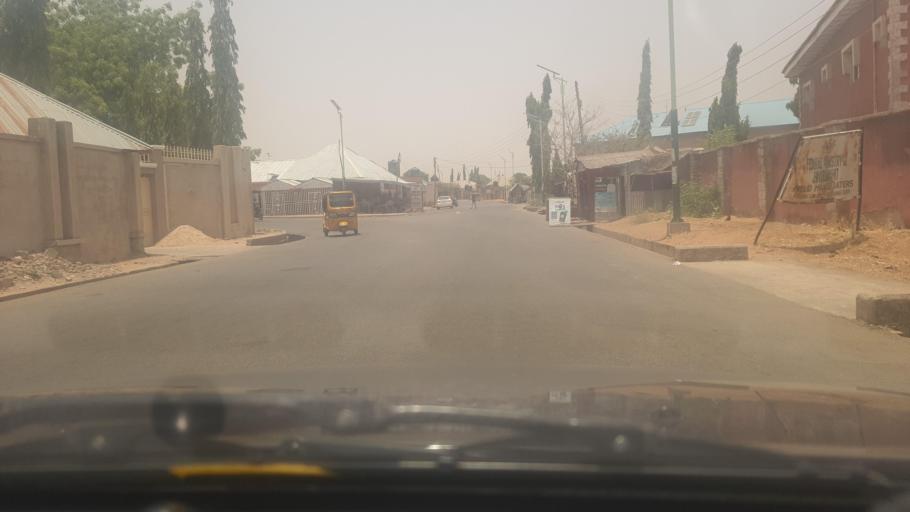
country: NG
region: Gombe
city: Gombe
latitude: 10.2985
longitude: 11.1515
